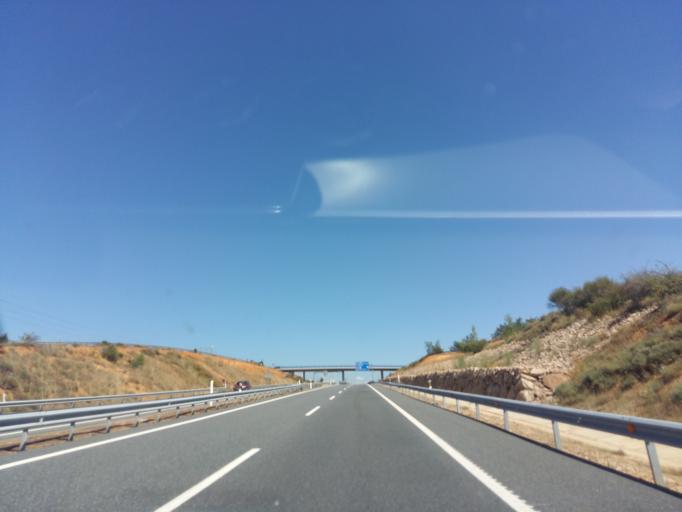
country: ES
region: Castille and Leon
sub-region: Provincia de Leon
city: Valverde de la Virgen
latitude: 42.5632
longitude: -5.6694
